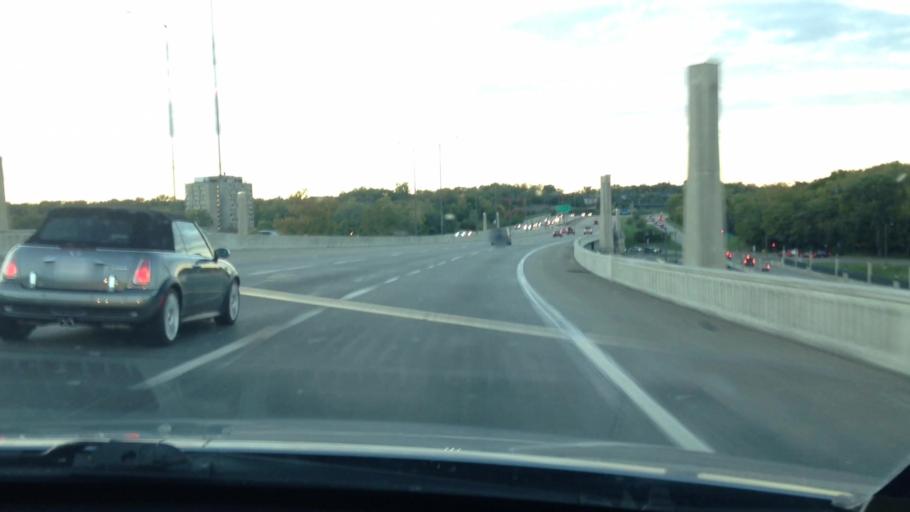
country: US
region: Kansas
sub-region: Johnson County
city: Westwood
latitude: 39.0402
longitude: -94.5586
